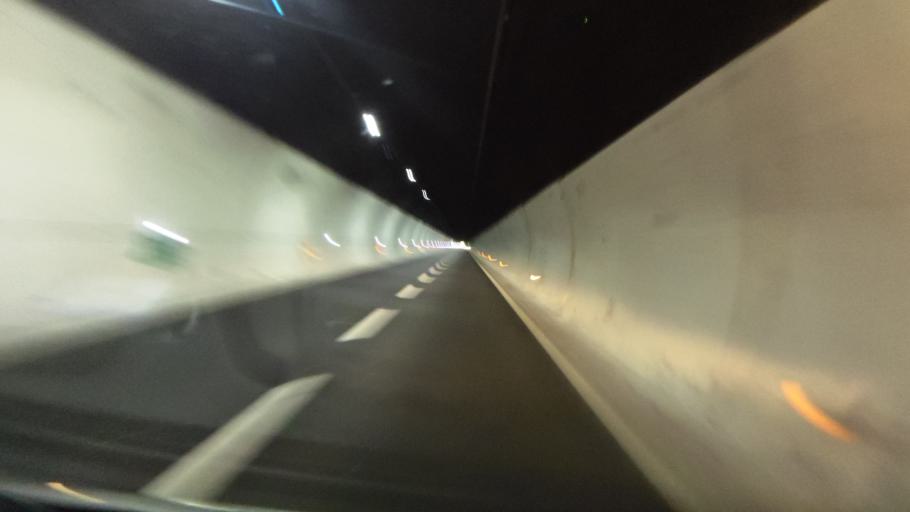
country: IT
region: Friuli Venezia Giulia
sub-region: Provincia di Udine
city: Pontebba
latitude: 46.4964
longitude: 13.3070
